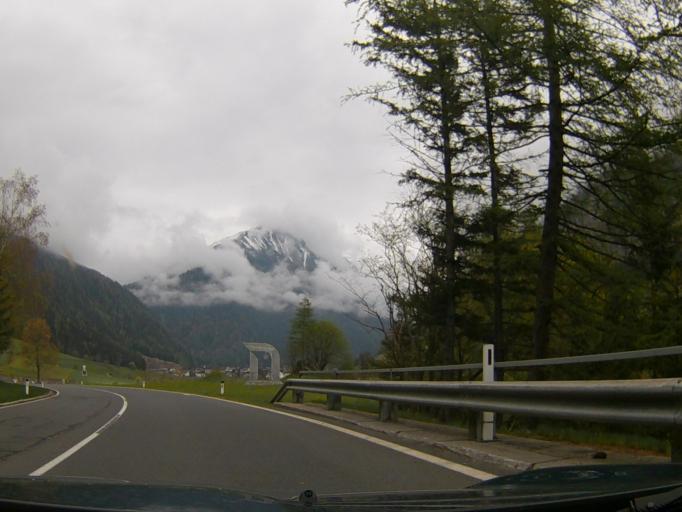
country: AT
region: Carinthia
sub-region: Politischer Bezirk Spittal an der Drau
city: Obervellach
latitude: 46.9725
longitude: 13.1809
